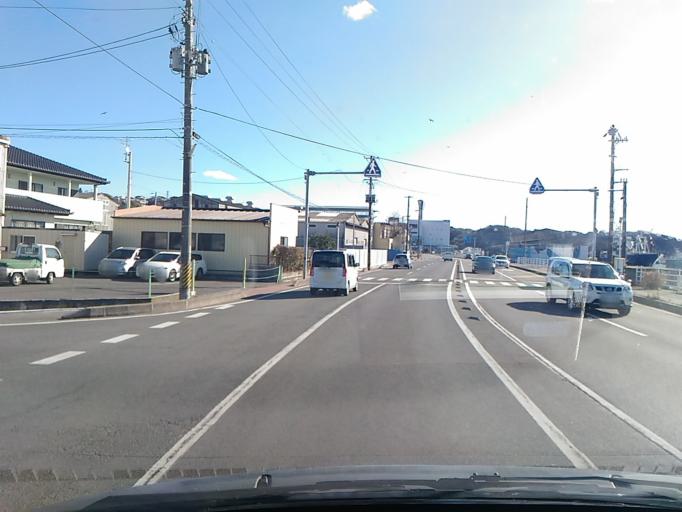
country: JP
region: Fukushima
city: Iwaki
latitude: 36.9456
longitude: 140.9097
